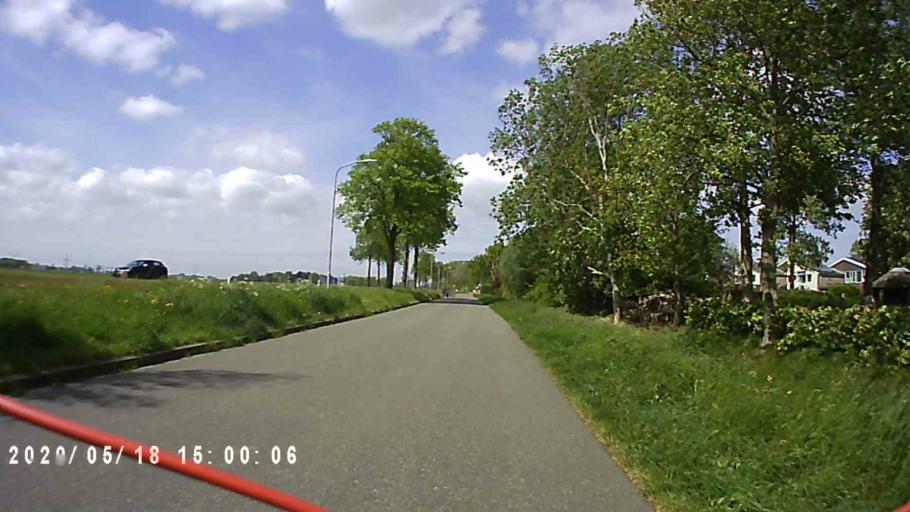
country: NL
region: Groningen
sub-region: Gemeente Winsum
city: Winsum
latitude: 53.3355
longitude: 6.5122
